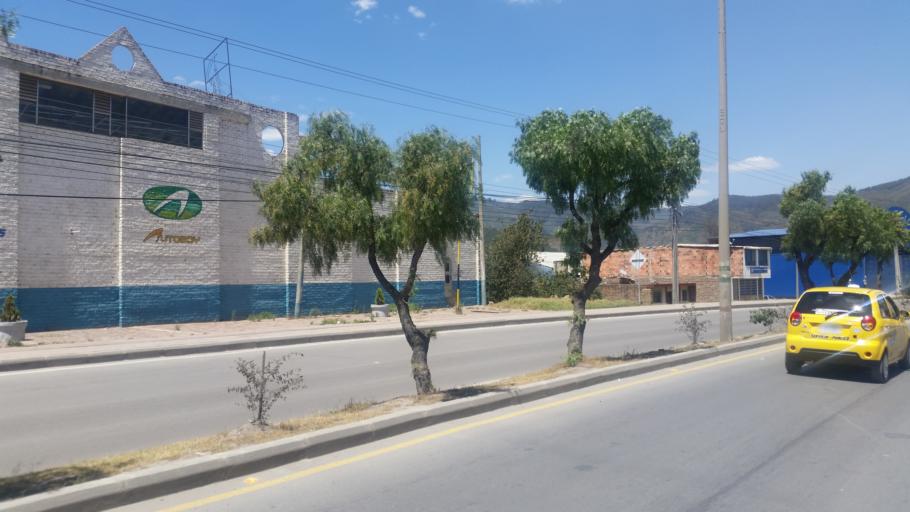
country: CO
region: Boyaca
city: Nobsa
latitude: 5.7479
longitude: -72.9147
